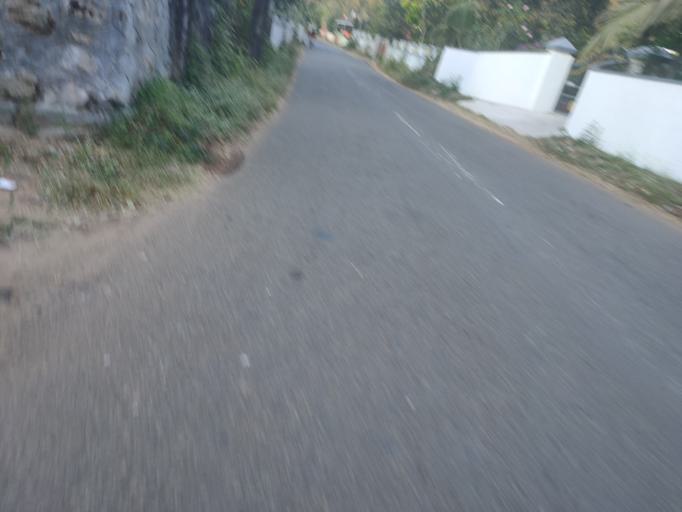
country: IN
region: Kerala
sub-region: Thrissur District
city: Kizhake Chalakudi
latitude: 10.2285
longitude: 76.3290
